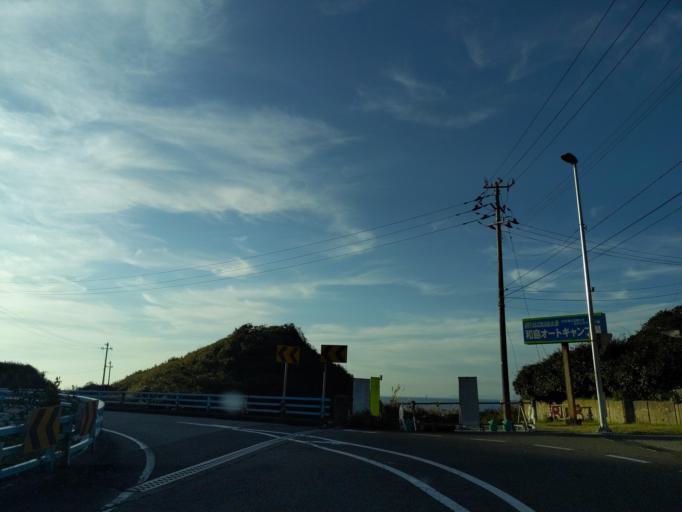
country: JP
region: Niigata
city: Nagaoka
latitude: 37.5768
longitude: 138.7288
